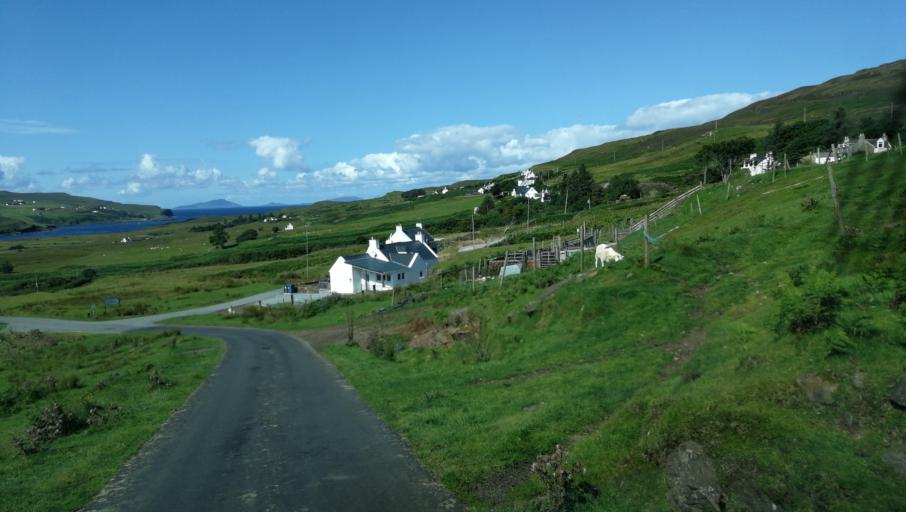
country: GB
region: Scotland
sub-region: Highland
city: Isle of Skye
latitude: 57.4503
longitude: -6.6959
